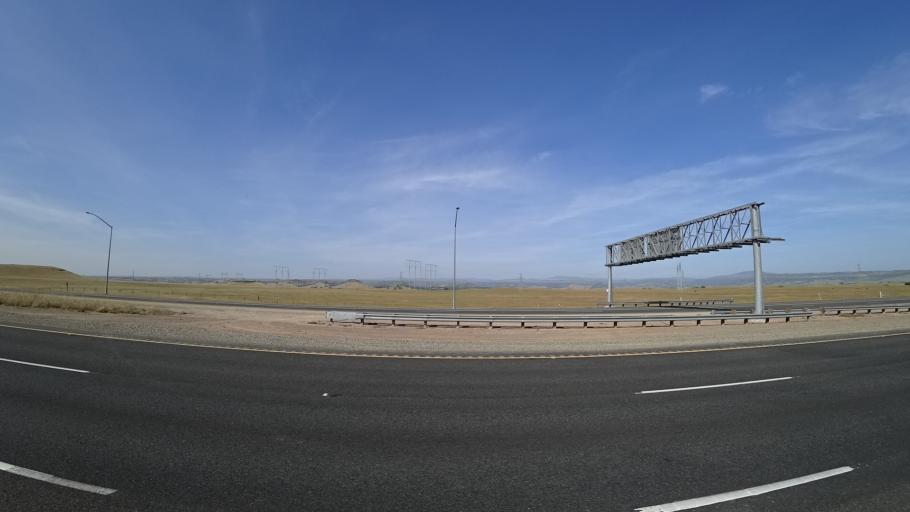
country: US
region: California
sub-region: Butte County
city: Durham
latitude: 39.6170
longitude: -121.6845
